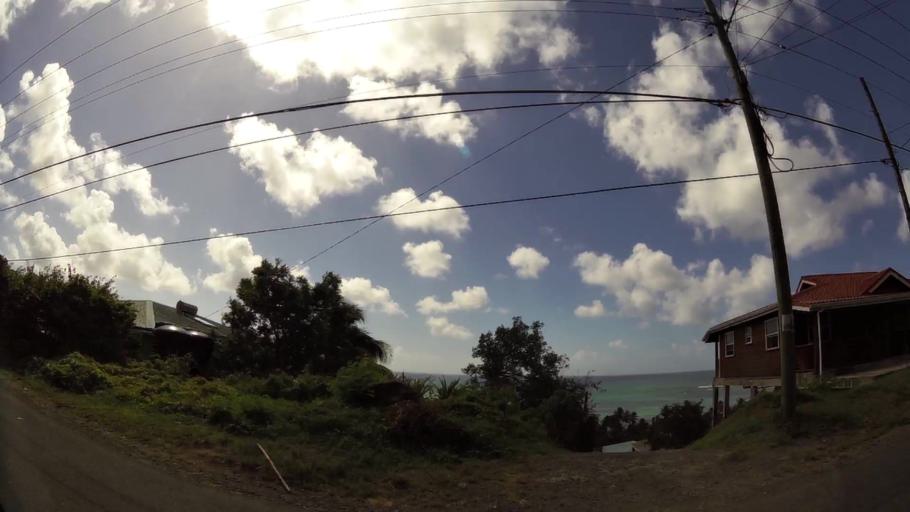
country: LC
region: Laborie Quarter
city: Laborie
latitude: 13.7538
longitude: -60.9971
